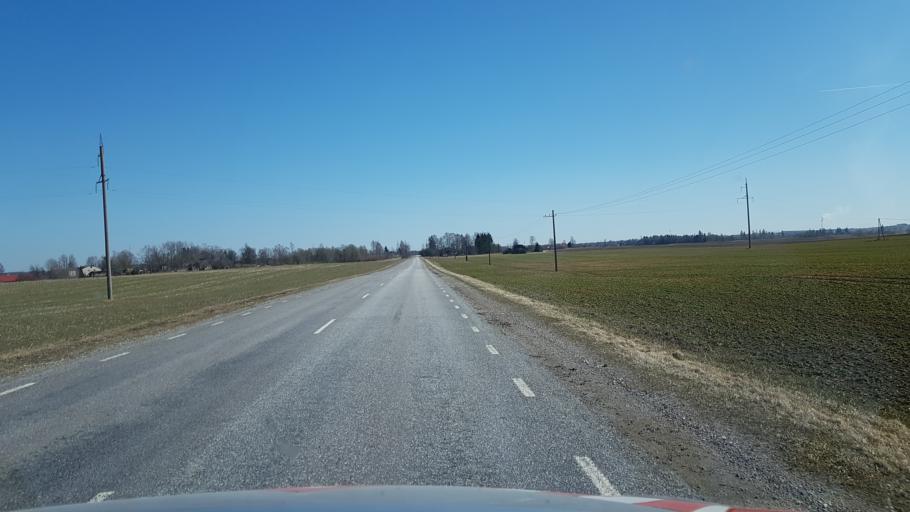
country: EE
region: Laeaene-Virumaa
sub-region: Vaeike-Maarja vald
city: Vaike-Maarja
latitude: 59.1506
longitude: 26.2226
